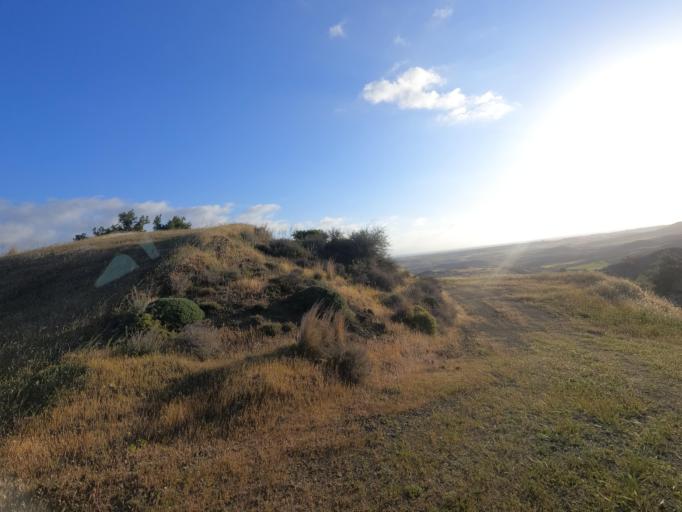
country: CY
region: Lefkosia
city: Astromeritis
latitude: 35.0687
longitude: 33.0360
